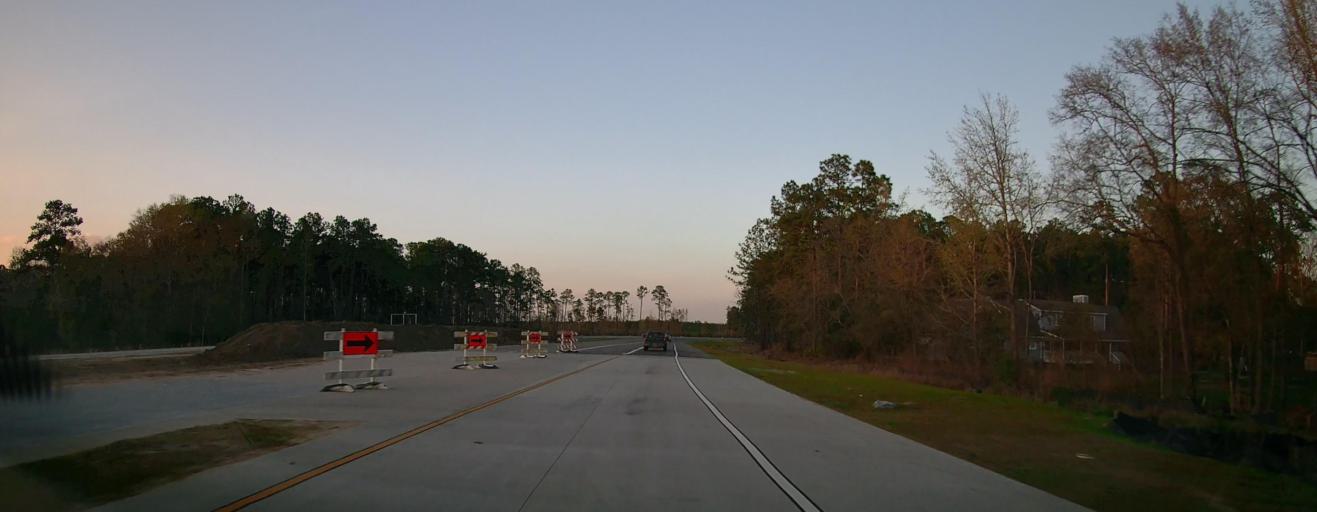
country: US
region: Georgia
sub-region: Chatham County
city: Bloomingdale
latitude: 32.1395
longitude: -81.3083
